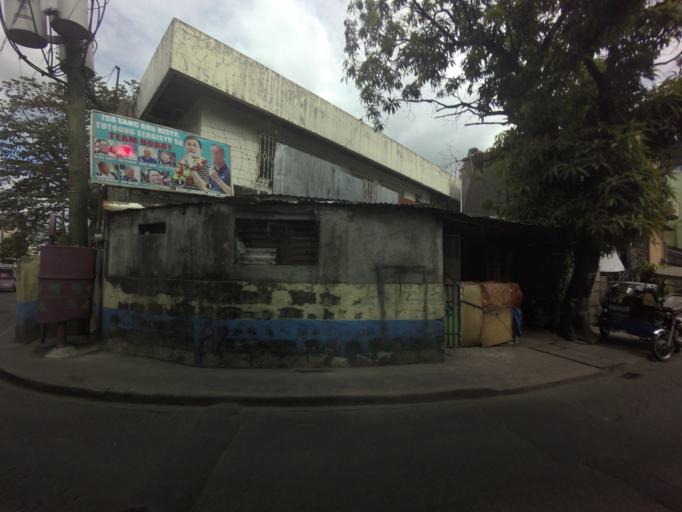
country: PH
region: Calabarzon
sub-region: Province of Rizal
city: Pateros
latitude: 14.5628
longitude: 121.0867
